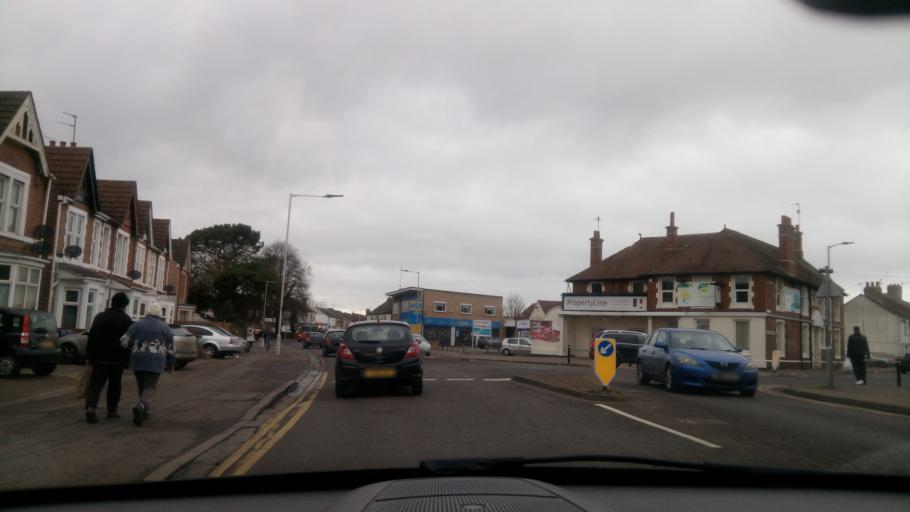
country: GB
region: England
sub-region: Peterborough
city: Peterborough
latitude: 52.5825
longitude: -0.2444
